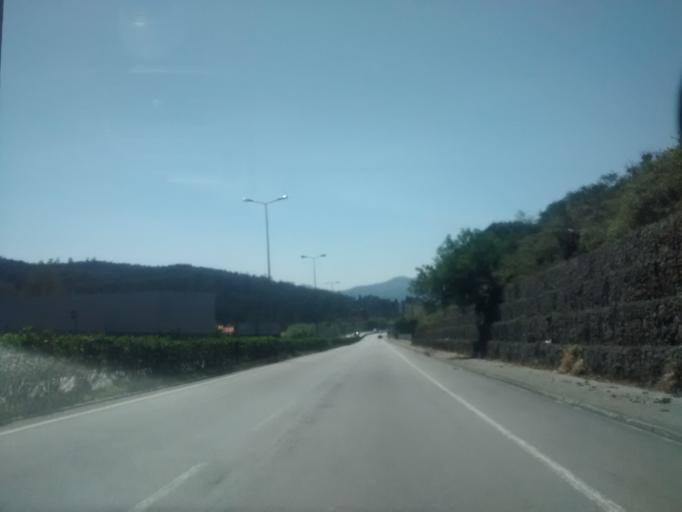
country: PT
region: Braga
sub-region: Braga
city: Braga
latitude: 41.5292
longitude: -8.4135
